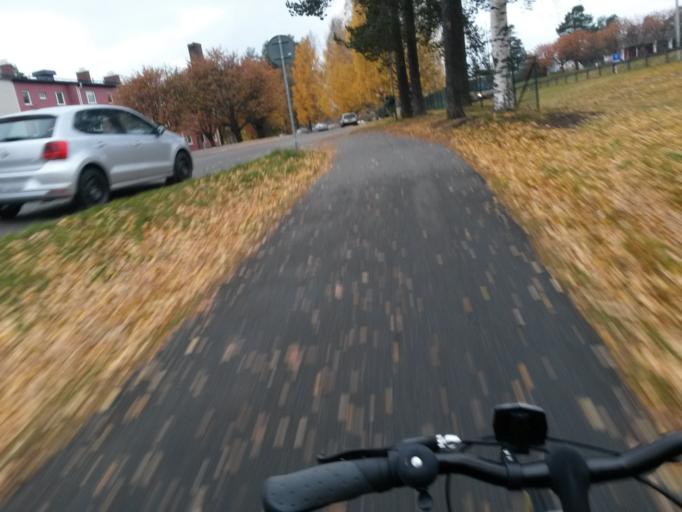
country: SE
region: Vaesterbotten
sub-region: Skelleftea Kommun
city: Skelleftea
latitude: 64.7596
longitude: 20.9714
